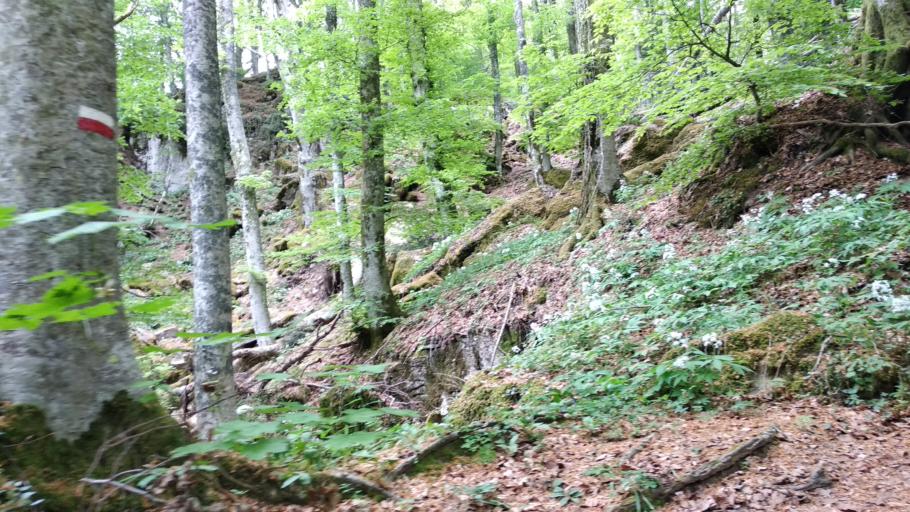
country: IT
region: Tuscany
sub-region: Province of Arezzo
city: Chiusi della Verna
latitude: 43.7119
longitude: 11.9284
